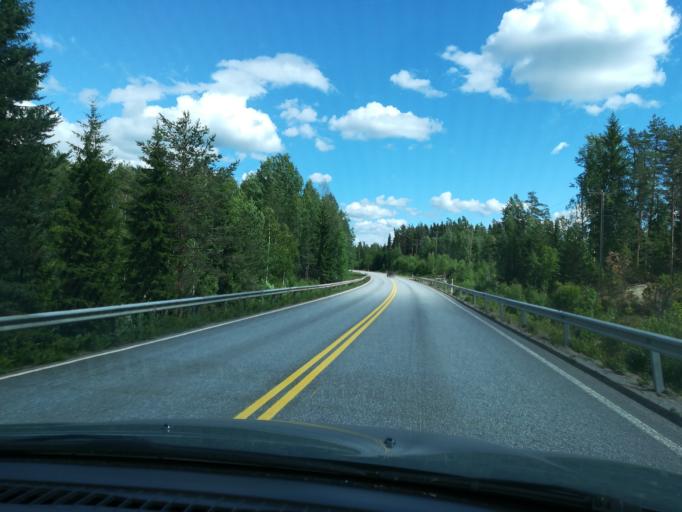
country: FI
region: Southern Savonia
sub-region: Mikkeli
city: Hirvensalmi
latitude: 61.6590
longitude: 26.9404
